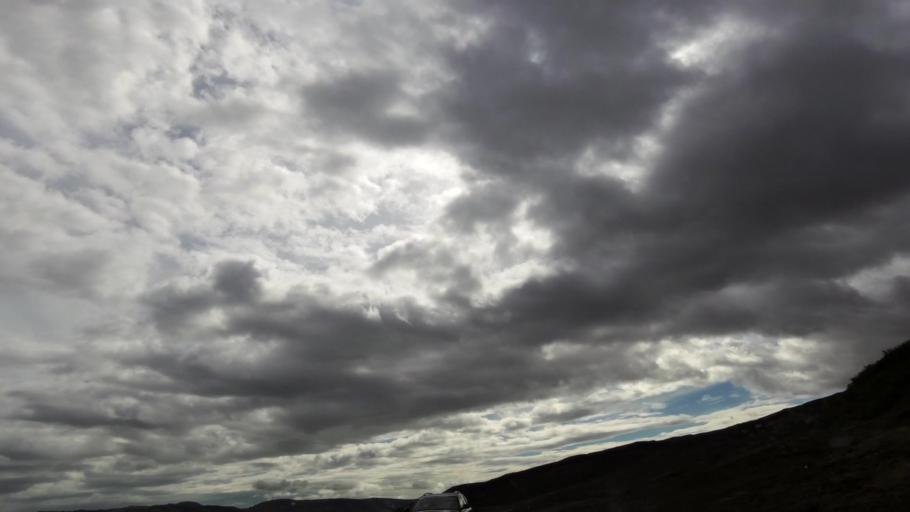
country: IS
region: West
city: Stykkisholmur
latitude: 65.5923
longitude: -22.1318
